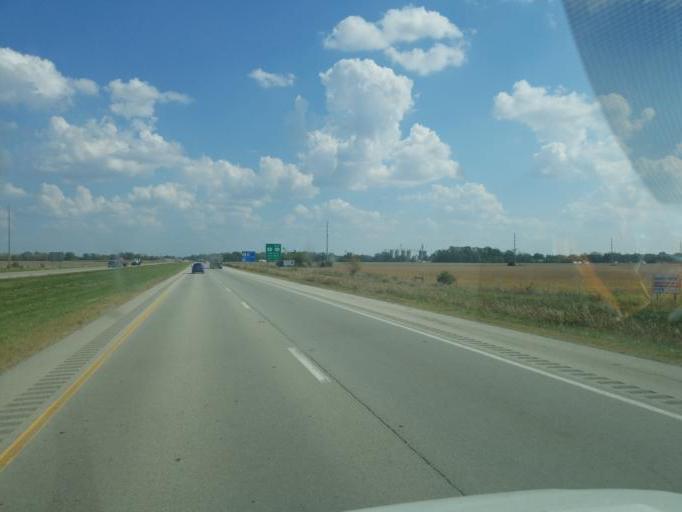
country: US
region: Ohio
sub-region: Van Wert County
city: Van Wert
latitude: 40.8889
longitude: -84.6028
